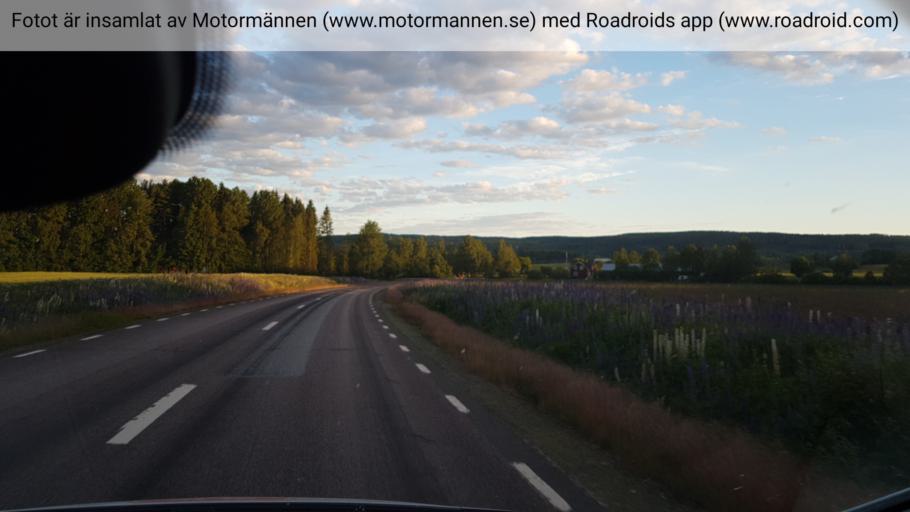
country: SE
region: Vaermland
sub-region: Sunne Kommun
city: Sunne
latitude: 59.7324
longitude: 13.1284
